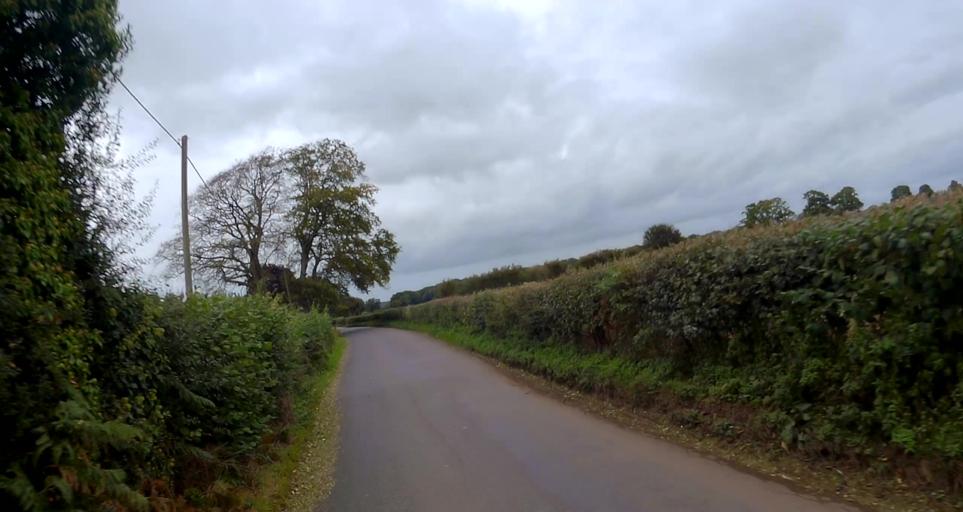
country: GB
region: England
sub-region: Hampshire
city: Four Marks
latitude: 51.1350
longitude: -1.0780
